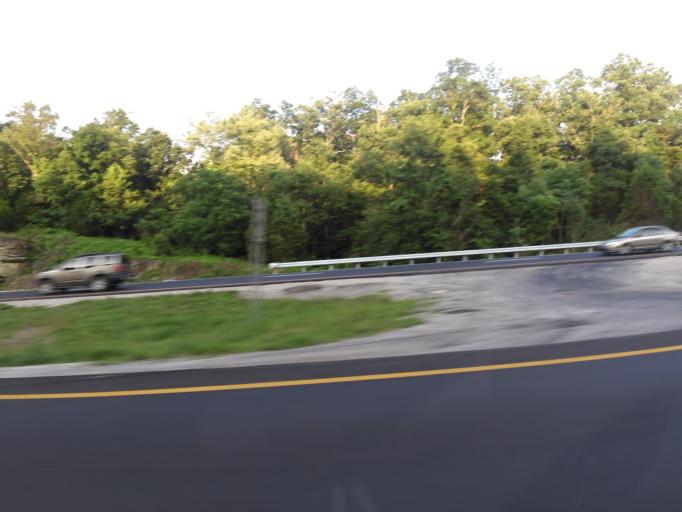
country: US
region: Kentucky
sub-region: Rockcastle County
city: Brodhead
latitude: 37.4616
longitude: -84.3357
